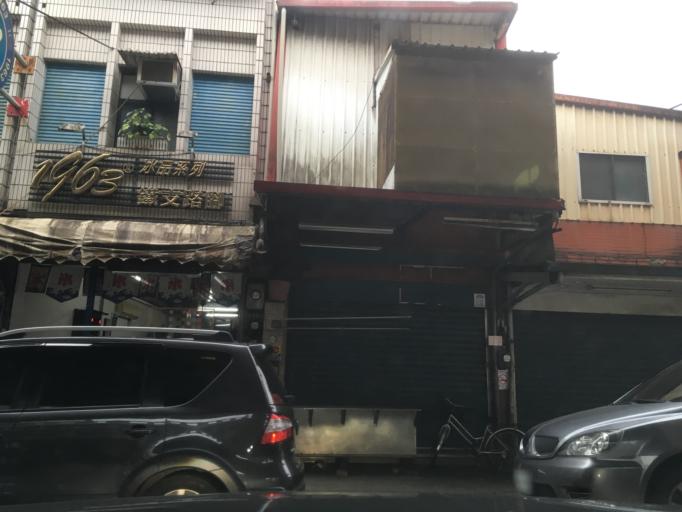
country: TW
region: Taiwan
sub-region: Yilan
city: Yilan
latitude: 24.7581
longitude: 121.7593
